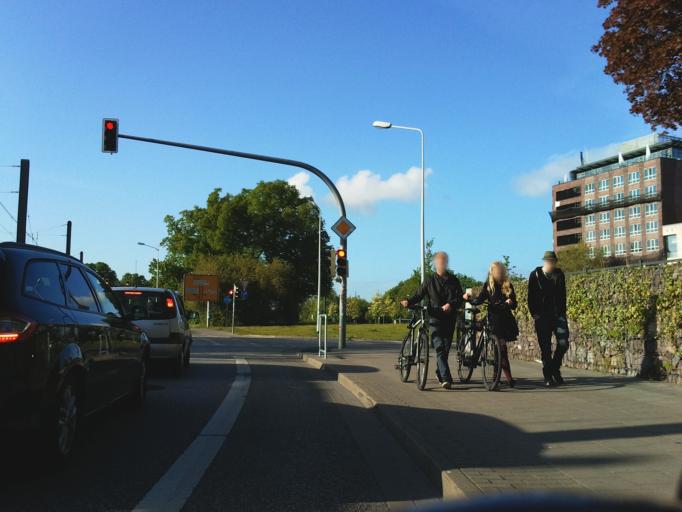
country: DE
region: Mecklenburg-Vorpommern
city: Rostock
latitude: 54.0883
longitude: 12.1278
